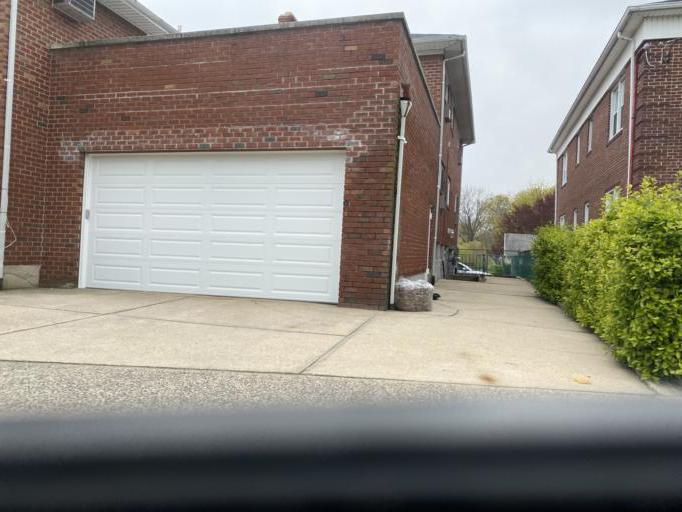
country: US
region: New York
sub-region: Nassau County
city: Floral Park
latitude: 40.7255
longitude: -73.7085
